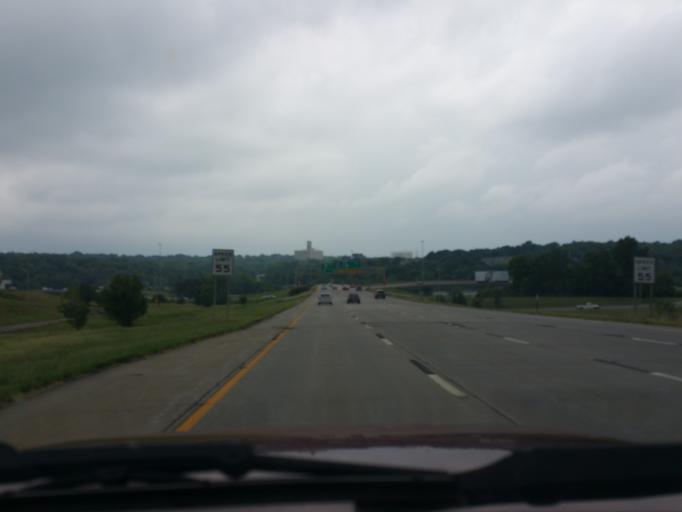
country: US
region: Kansas
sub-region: Johnson County
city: Merriam
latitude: 39.0440
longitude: -94.6769
